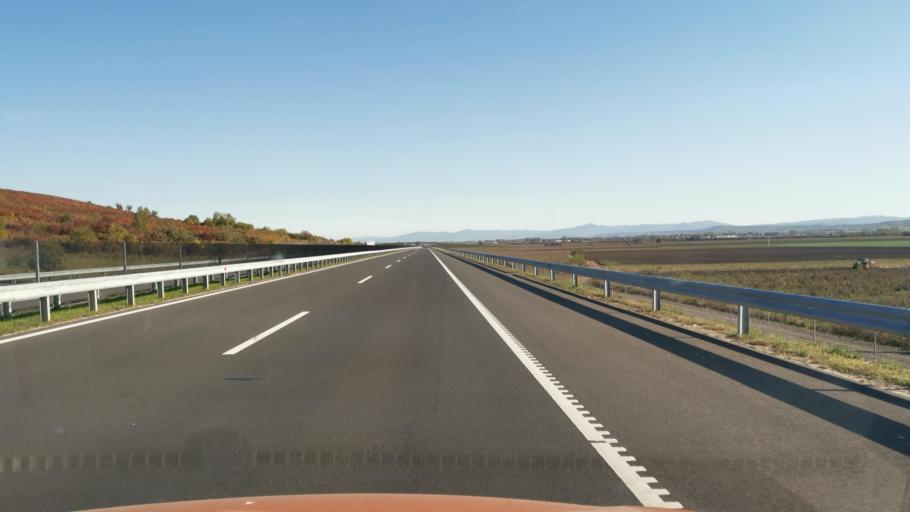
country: HU
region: Borsod-Abauj-Zemplen
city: Aszalo
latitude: 48.2321
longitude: 20.9533
